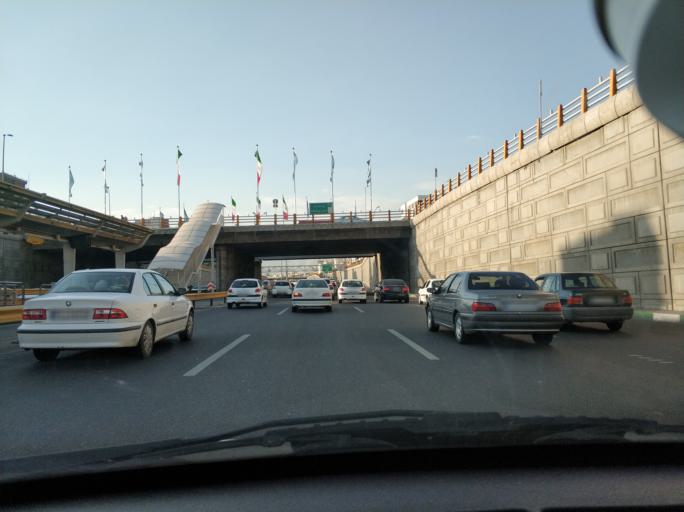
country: IR
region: Tehran
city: Tehran
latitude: 35.6963
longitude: 51.4569
